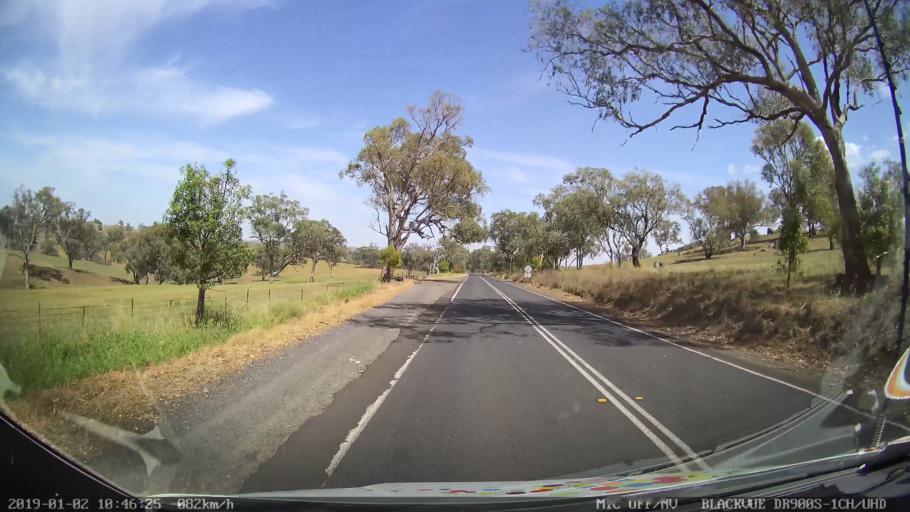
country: AU
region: New South Wales
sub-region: Cootamundra
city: Cootamundra
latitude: -34.7516
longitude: 148.2876
